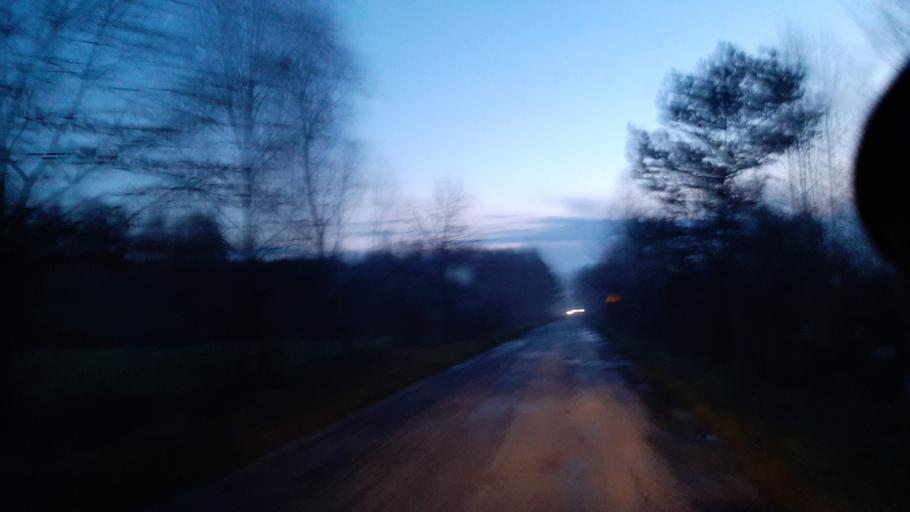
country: PL
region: Lublin Voivodeship
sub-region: Powiat lubartowski
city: Firlej
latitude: 51.5277
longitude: 22.5016
